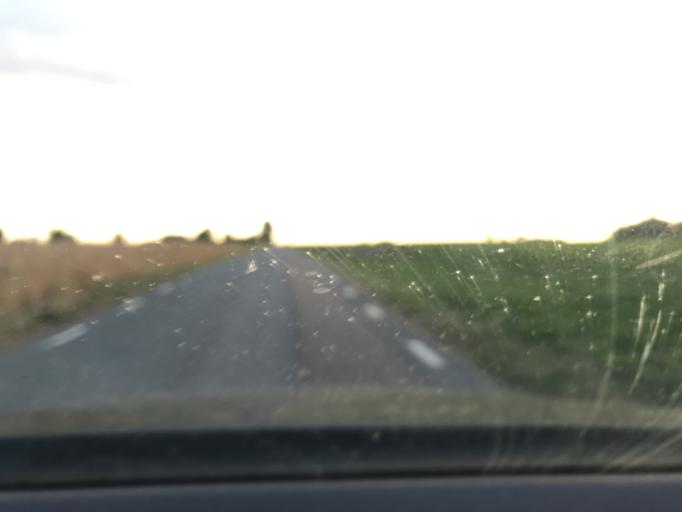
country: SE
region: Skane
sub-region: Simrishamns Kommun
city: Simrishamn
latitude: 55.4425
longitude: 14.2228
